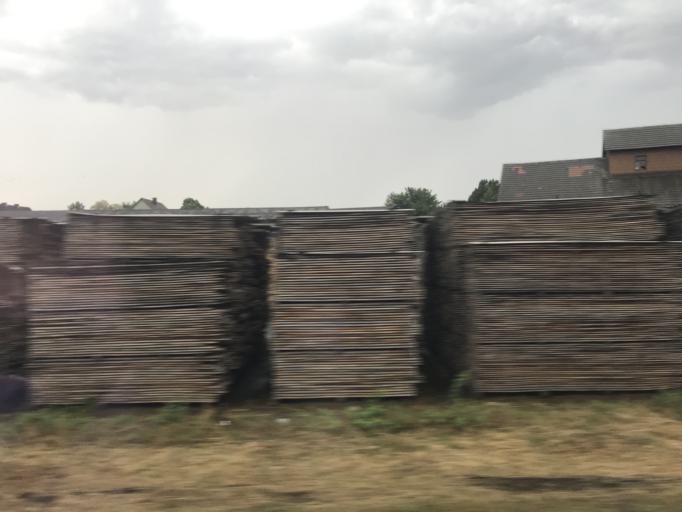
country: DE
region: Bavaria
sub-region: Regierungsbezirk Unterfranken
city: Bergtheim
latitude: 49.9008
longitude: 10.0765
